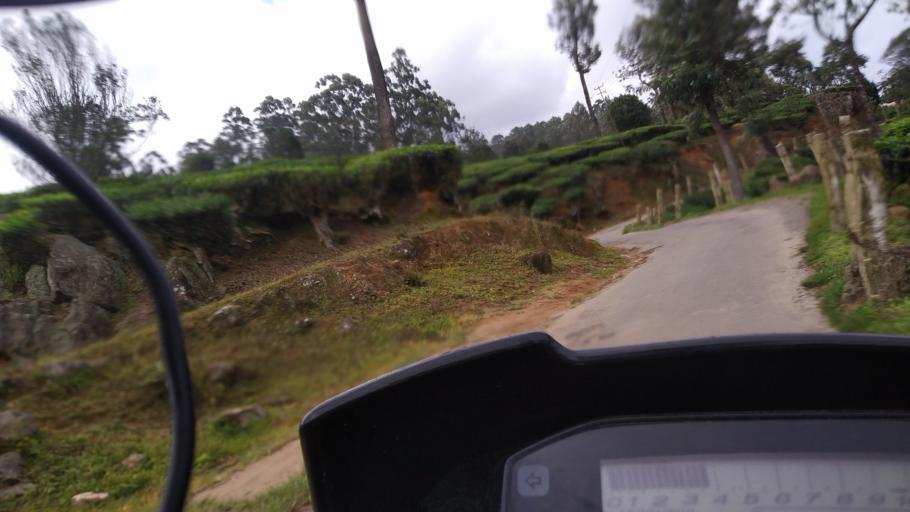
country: IN
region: Kerala
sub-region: Idukki
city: Munnar
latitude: 10.0331
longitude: 77.1678
